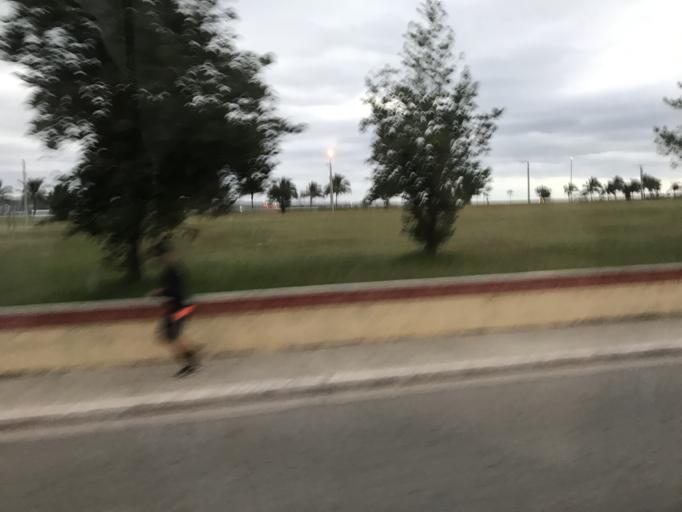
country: CU
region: Matanzas
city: Matanzas
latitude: 23.0363
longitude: -81.5624
